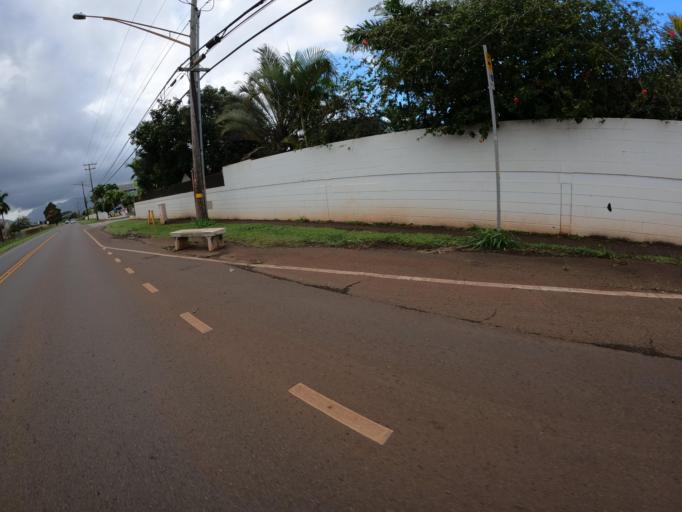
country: US
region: Hawaii
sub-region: Honolulu County
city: Whitmore Village
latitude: 21.5100
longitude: -158.0246
